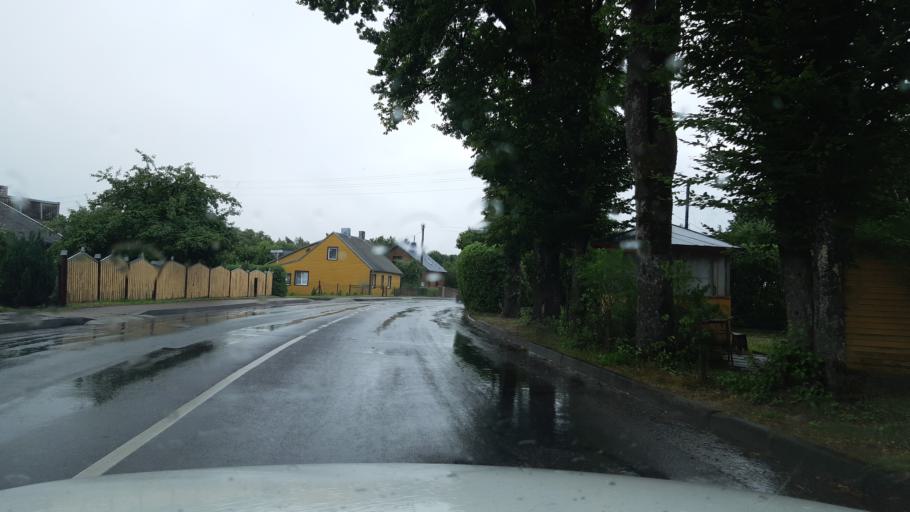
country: LT
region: Taurages apskritis
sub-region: Jurbarkas
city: Jurbarkas
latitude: 55.0807
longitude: 22.7591
